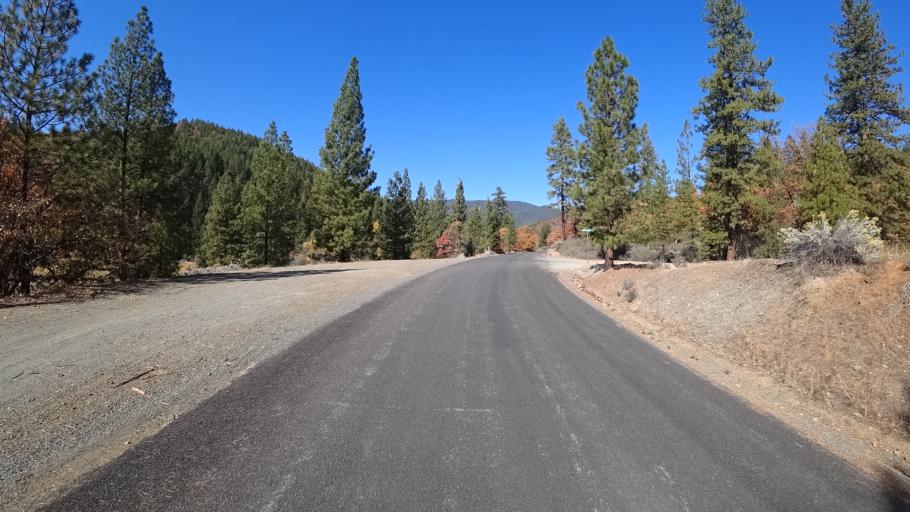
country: US
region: California
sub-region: Siskiyou County
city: Yreka
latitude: 41.6801
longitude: -122.8497
